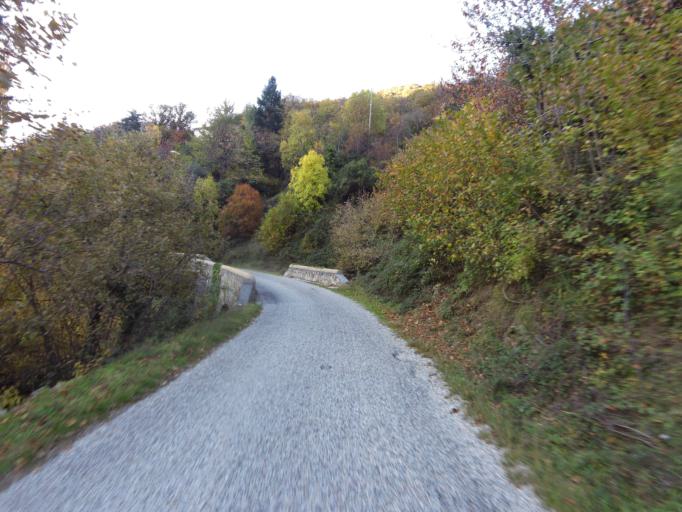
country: FR
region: Rhone-Alpes
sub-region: Departement de l'Ardeche
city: Les Vans
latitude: 44.5279
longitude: 4.0833
